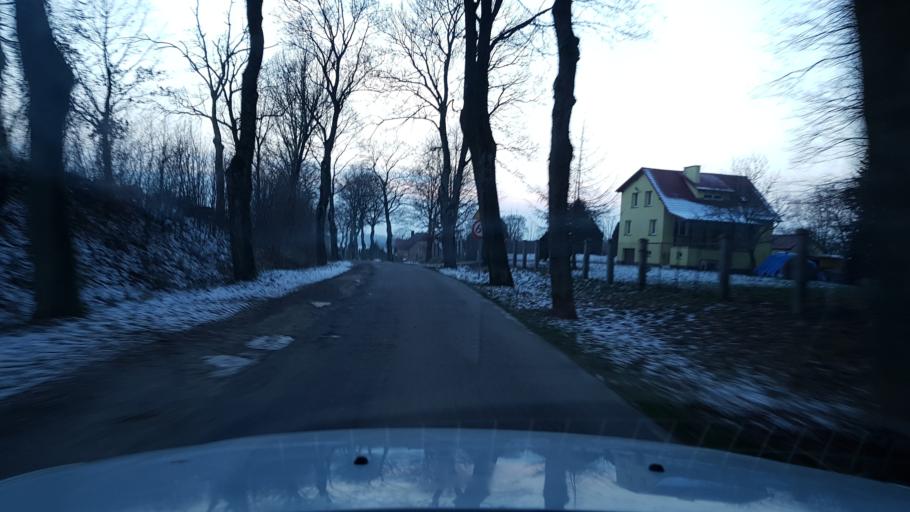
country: PL
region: West Pomeranian Voivodeship
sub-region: Powiat swidwinski
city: Slawoborze
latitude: 53.9706
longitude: 15.7659
